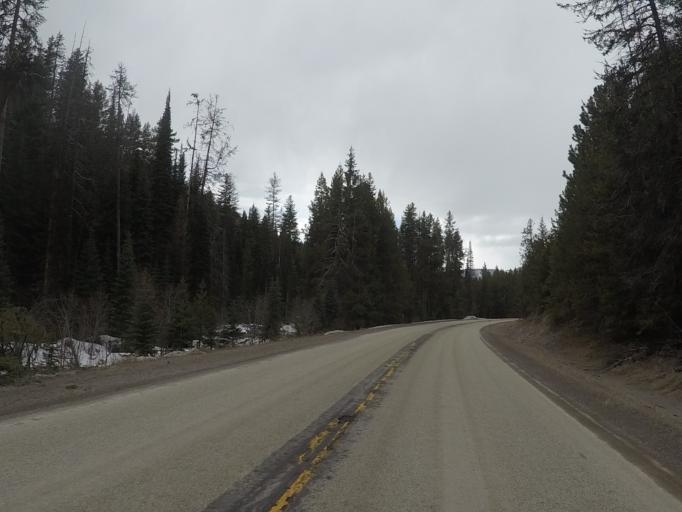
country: US
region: Montana
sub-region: Missoula County
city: Frenchtown
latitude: 46.6971
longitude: -114.5434
